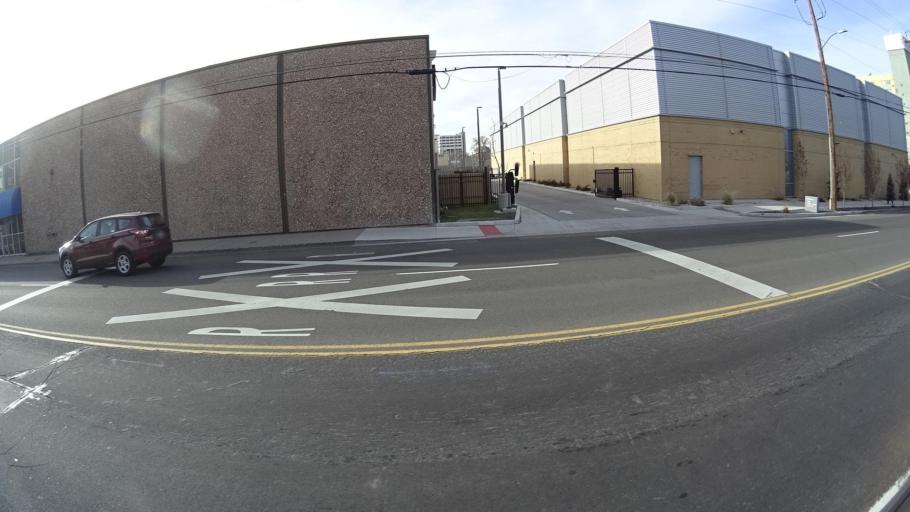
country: US
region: Nevada
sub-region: Washoe County
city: Reno
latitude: 39.5334
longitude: -119.8104
